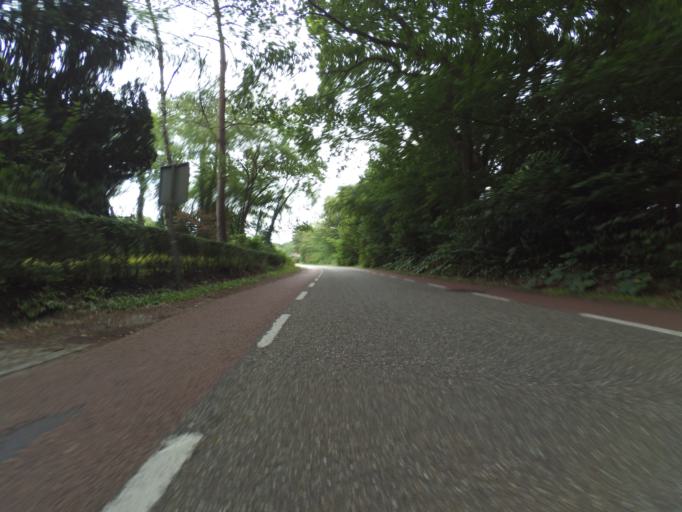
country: NL
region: Utrecht
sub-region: Gemeente Utrechtse Heuvelrug
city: Overberg
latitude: 52.0308
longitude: 5.4934
